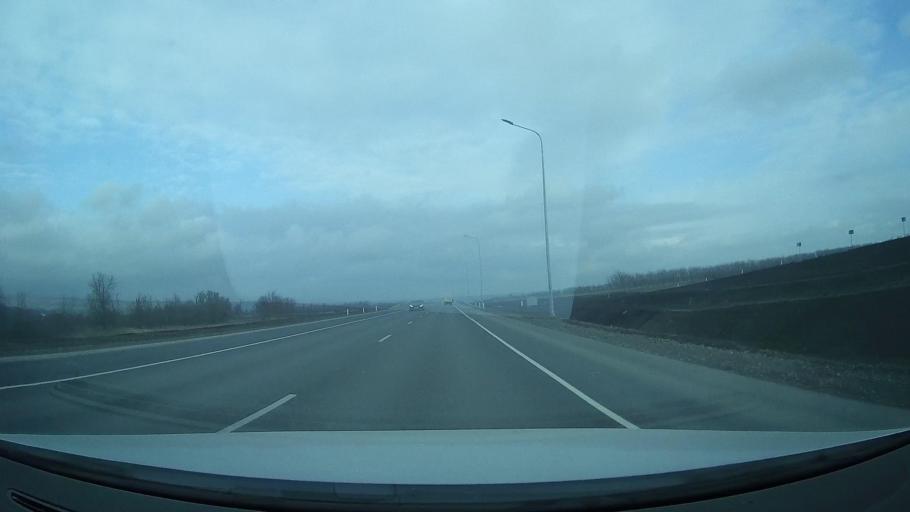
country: RU
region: Rostov
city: Grushevskaya
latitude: 47.4248
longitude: 39.8647
